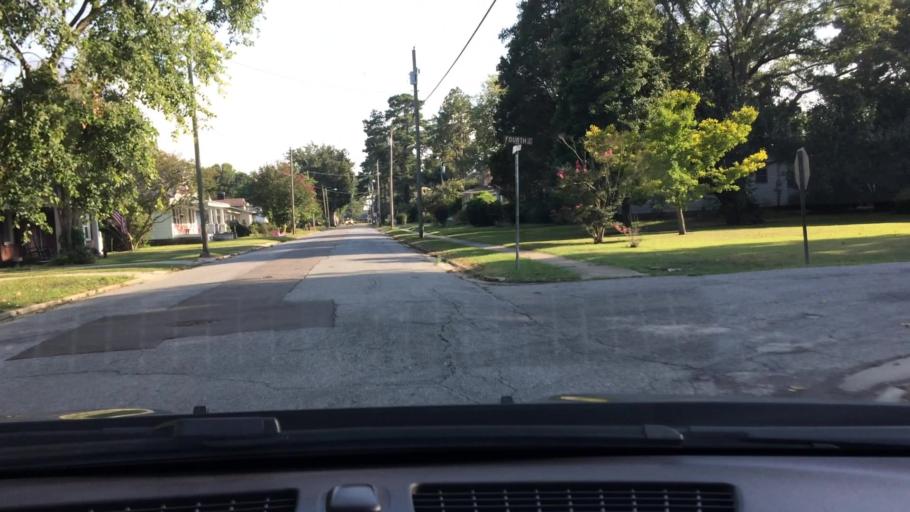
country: US
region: North Carolina
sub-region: Pitt County
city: Ayden
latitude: 35.4705
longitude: -77.4230
